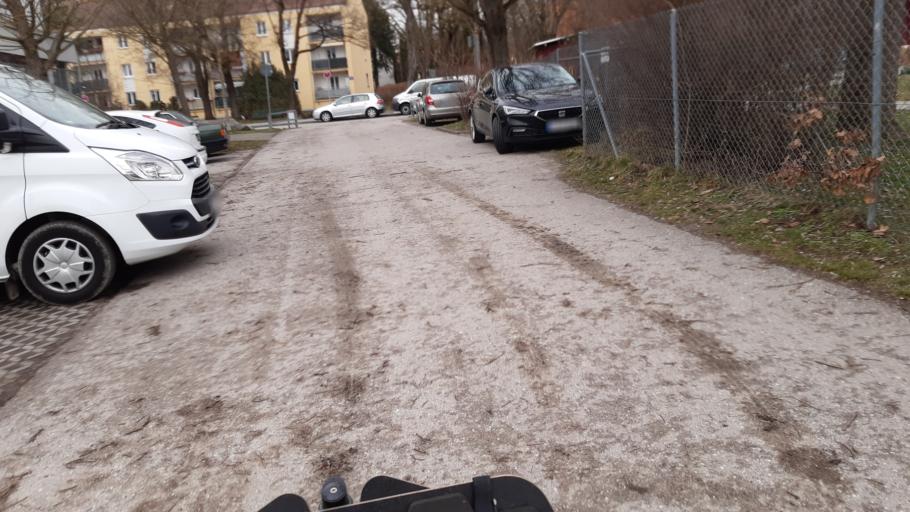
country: DE
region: Bavaria
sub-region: Upper Bavaria
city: Karlsfeld
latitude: 48.2134
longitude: 11.4884
